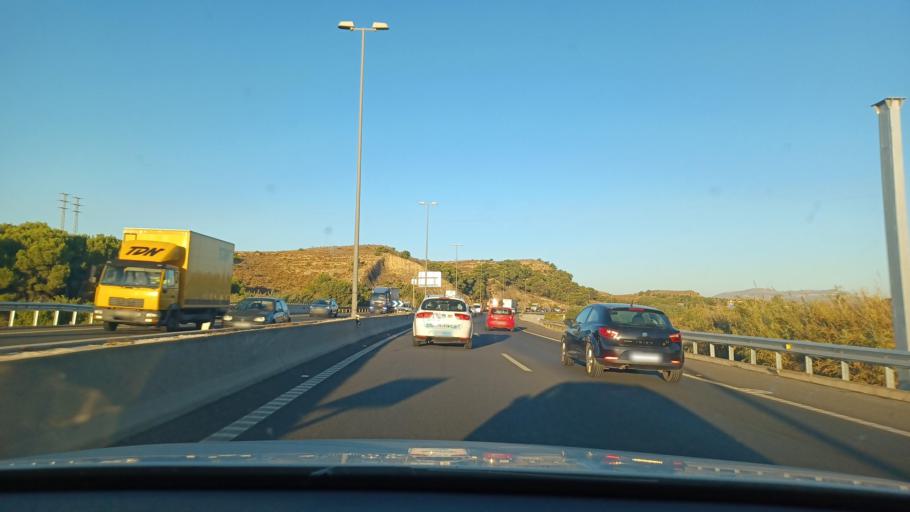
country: ES
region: Valencia
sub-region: Provincia de Alicante
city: San Juan de Alicante
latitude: 38.3796
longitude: -0.4650
